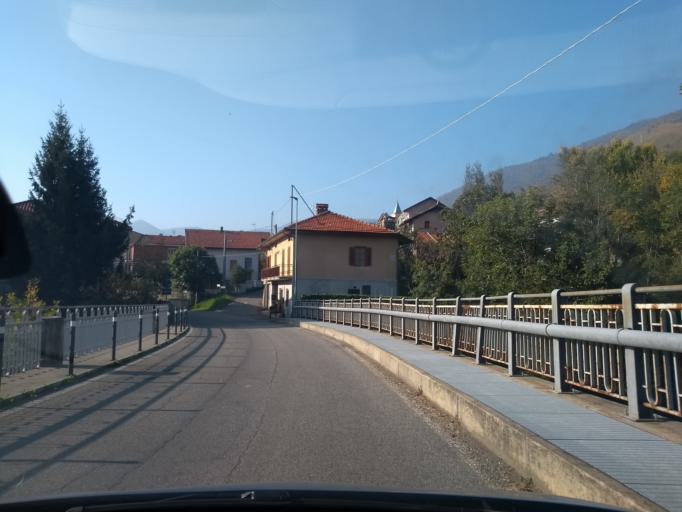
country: IT
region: Piedmont
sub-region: Provincia di Torino
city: Vallo Torinese
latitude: 45.2265
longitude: 7.4973
